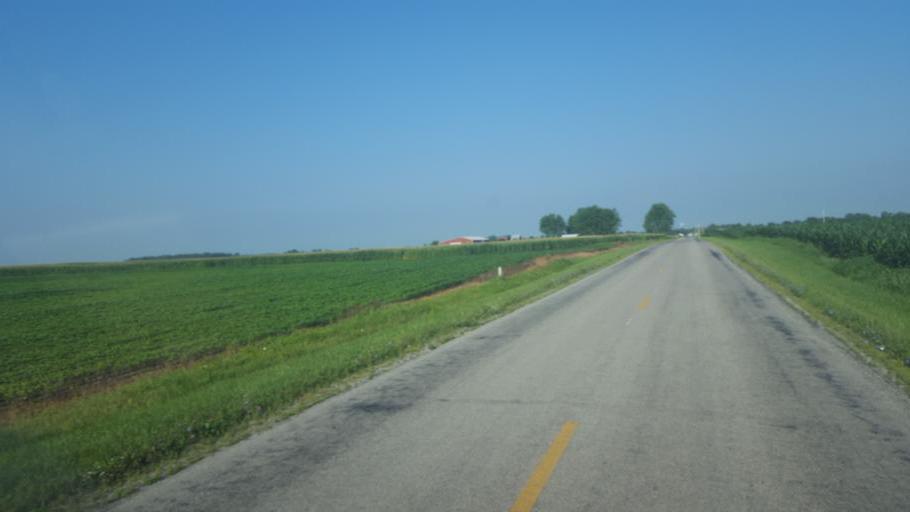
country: US
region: Ohio
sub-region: Hardin County
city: Kenton
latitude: 40.5356
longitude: -83.4978
